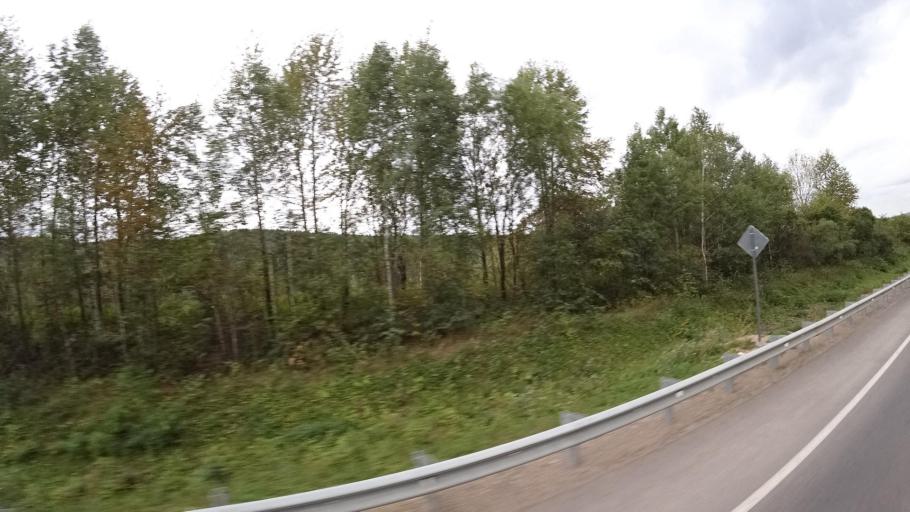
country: RU
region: Jewish Autonomous Oblast
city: Khingansk
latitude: 48.9879
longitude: 131.1326
